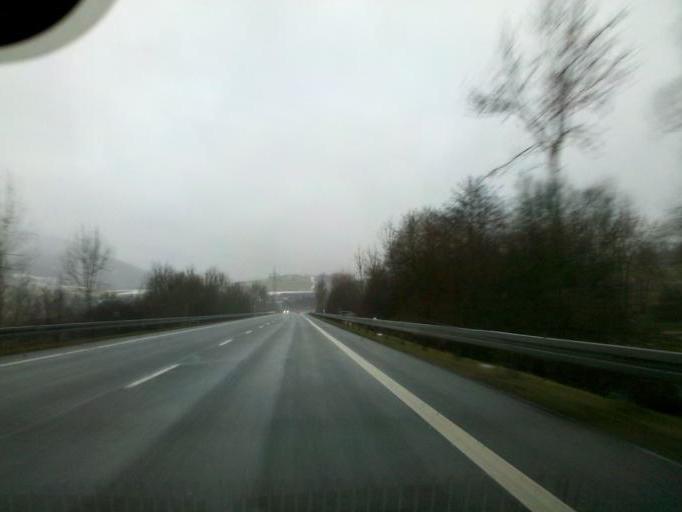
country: DE
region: Hesse
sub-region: Regierungsbezirk Giessen
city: Siegbach
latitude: 50.8115
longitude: 8.3580
